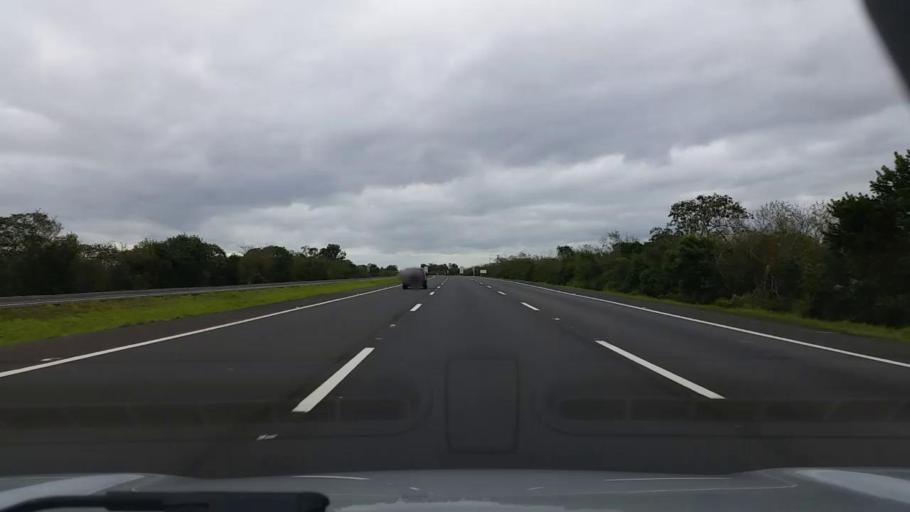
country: BR
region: Rio Grande do Sul
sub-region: Rolante
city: Rolante
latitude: -29.8838
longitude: -50.5620
